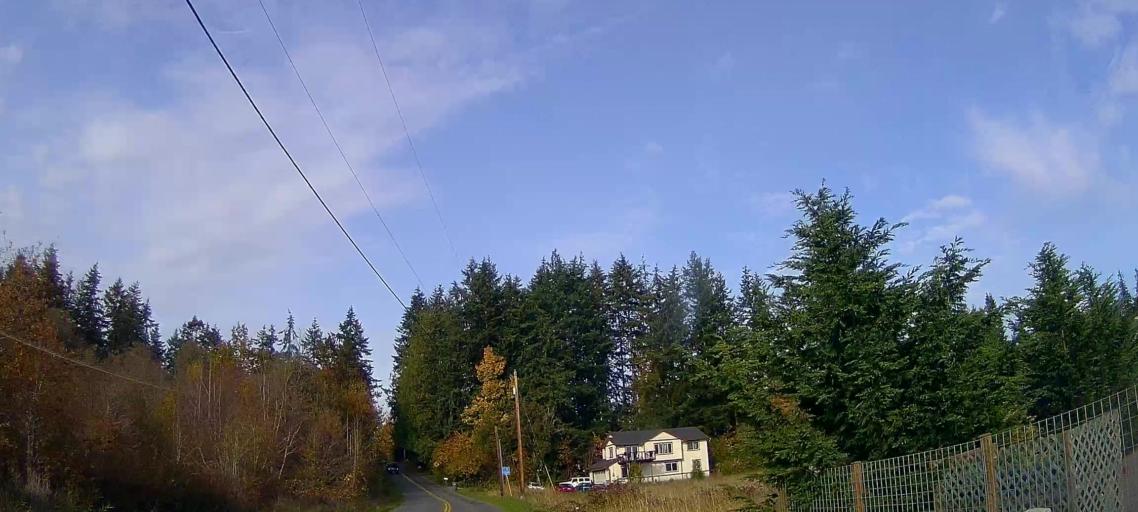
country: US
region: Washington
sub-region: Snohomish County
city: Stanwood
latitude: 48.2476
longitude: -122.3413
